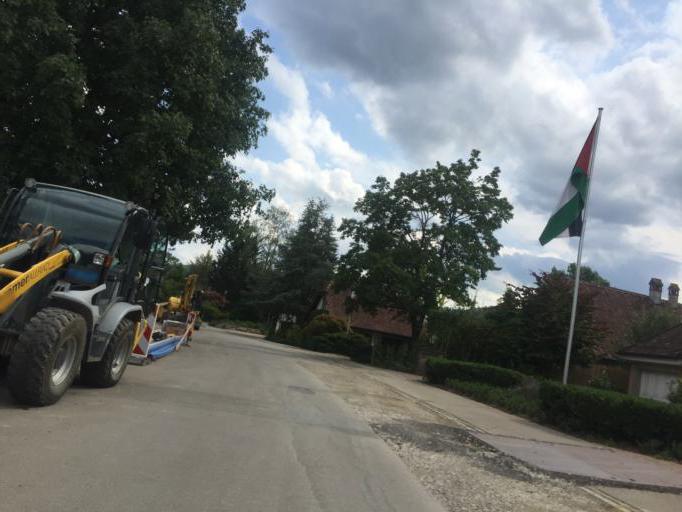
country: CH
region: Bern
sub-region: Bern-Mittelland District
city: Muri
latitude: 46.9298
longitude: 7.4754
